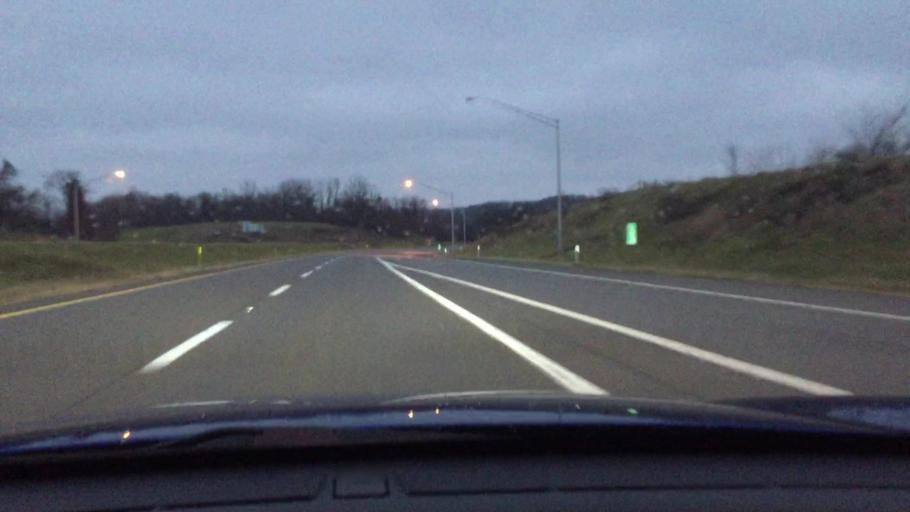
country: US
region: Pennsylvania
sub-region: Allegheny County
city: Imperial
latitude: 40.4540
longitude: -80.3059
